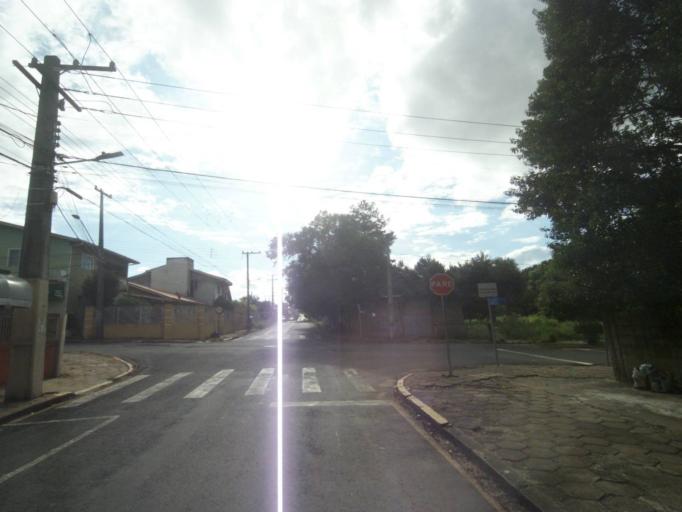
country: BR
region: Parana
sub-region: Telemaco Borba
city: Telemaco Borba
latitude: -24.3351
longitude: -50.6148
